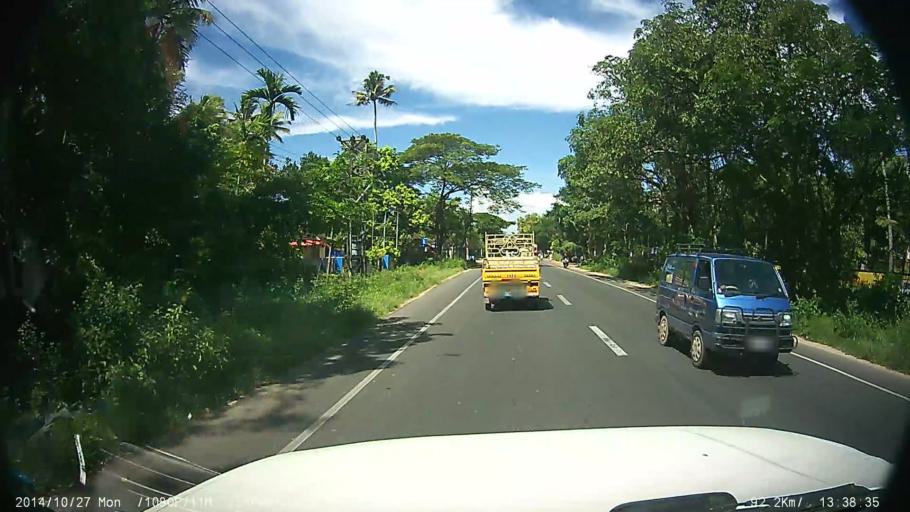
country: IN
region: Kerala
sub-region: Alappuzha
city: Shertallai
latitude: 9.6201
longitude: 76.3315
